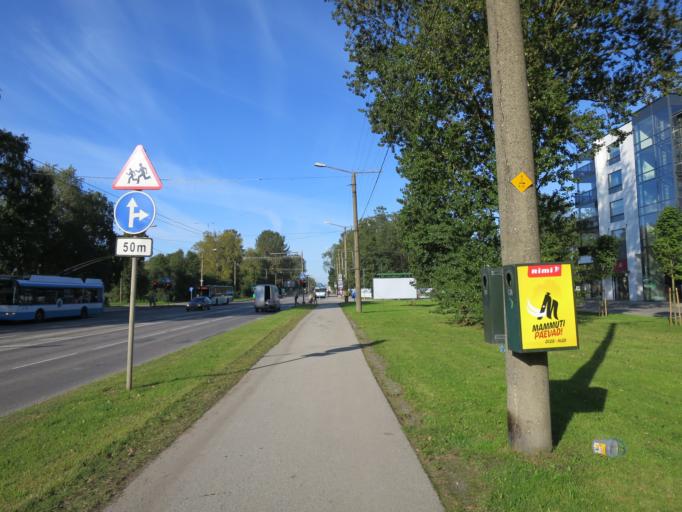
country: EE
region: Harju
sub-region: Tallinna linn
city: Tallinn
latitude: 59.4188
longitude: 24.7124
